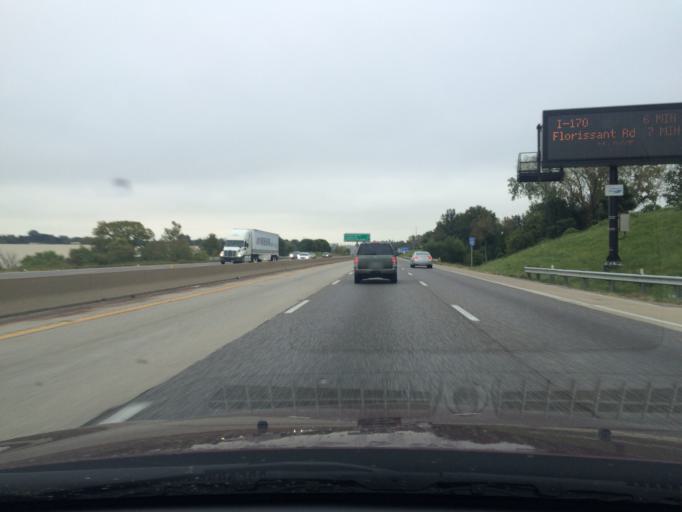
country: US
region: Missouri
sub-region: Saint Louis County
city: Bridgeton
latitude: 38.7449
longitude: -90.4264
